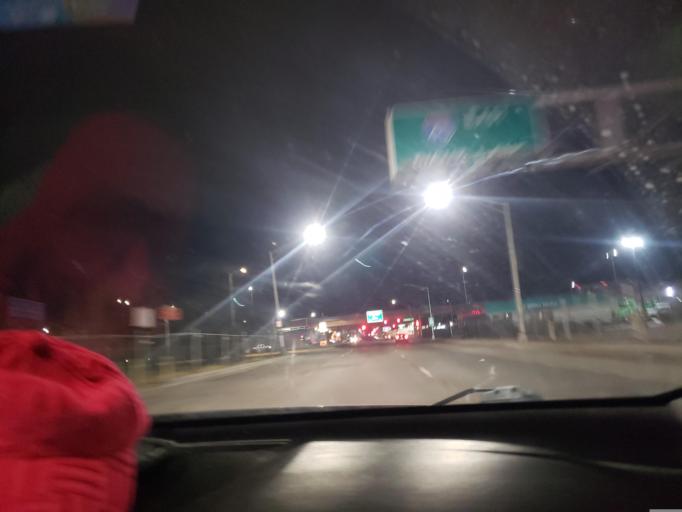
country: US
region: New Mexico
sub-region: Bernalillo County
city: Albuquerque
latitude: 35.1039
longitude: -106.6455
